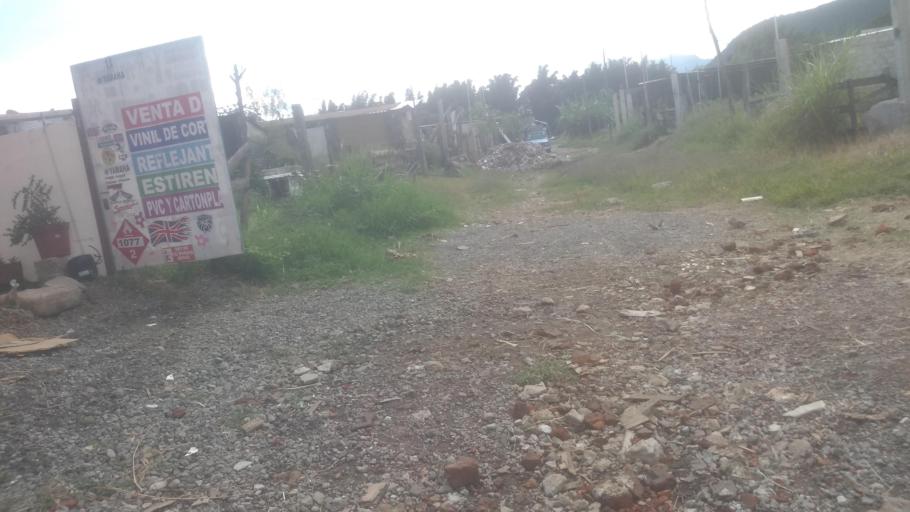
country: MX
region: Veracruz
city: Ixtac Zoquitlan
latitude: 18.8814
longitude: -97.0626
